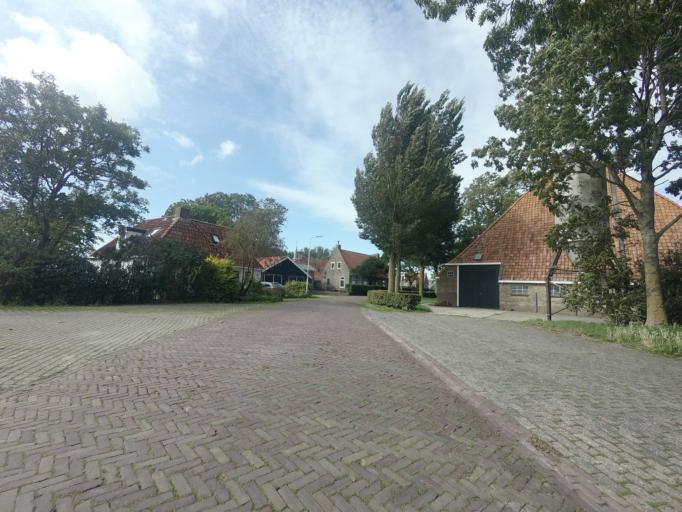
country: NL
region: Friesland
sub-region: Sudwest Fryslan
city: Bolsward
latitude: 53.0148
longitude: 5.5195
